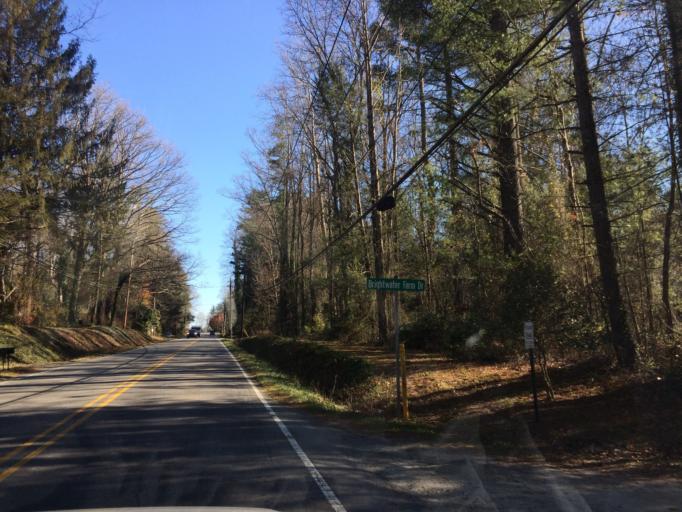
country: US
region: North Carolina
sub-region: Henderson County
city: Laurel Park
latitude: 35.3327
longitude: -82.5228
